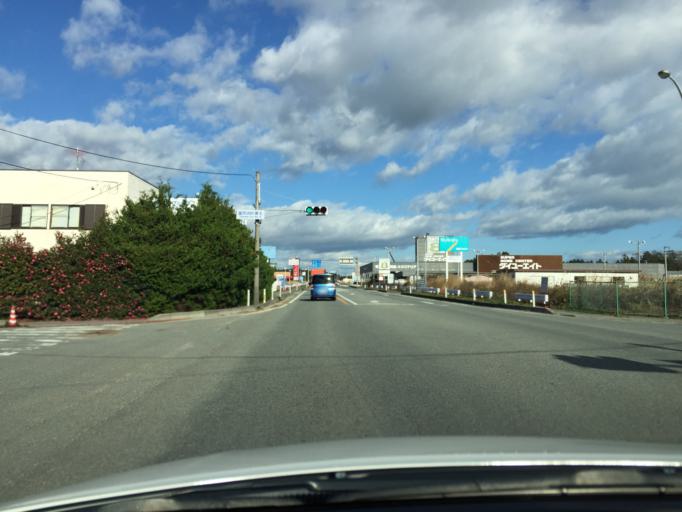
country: JP
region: Fukushima
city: Namie
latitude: 37.3569
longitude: 141.0103
